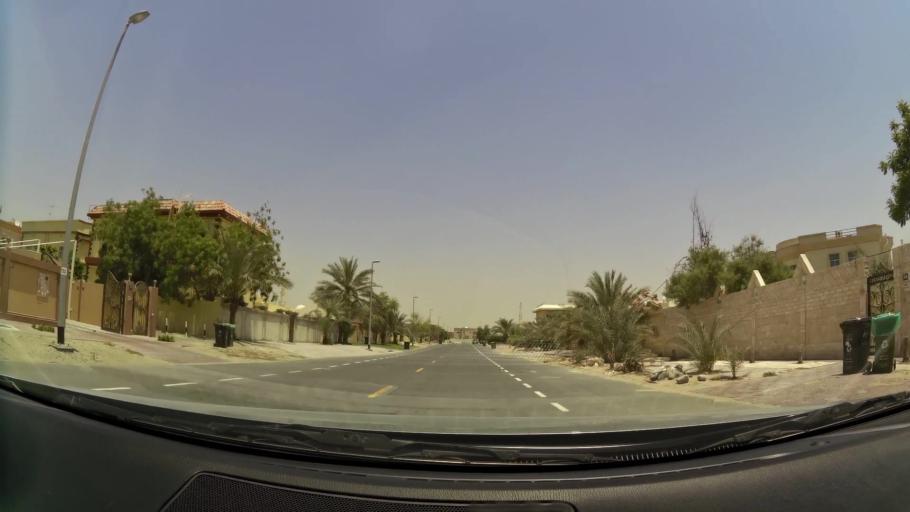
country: AE
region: Dubai
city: Dubai
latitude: 25.0899
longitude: 55.1924
